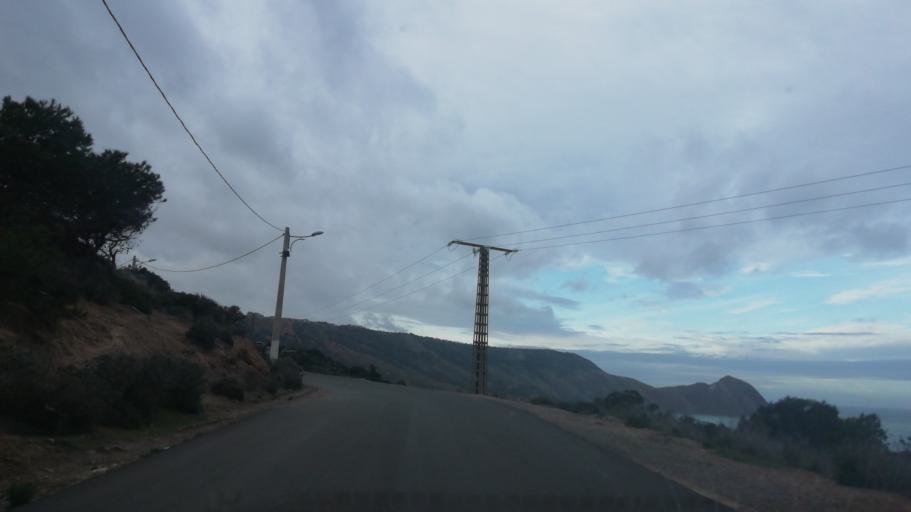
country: DZ
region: Oran
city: Bir el Djir
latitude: 35.7702
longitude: -0.5216
